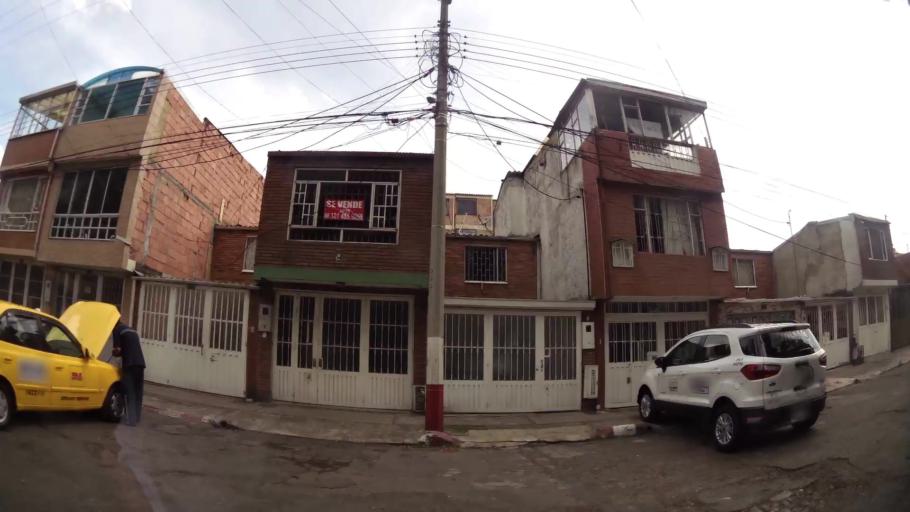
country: CO
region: Bogota D.C.
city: Bogota
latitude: 4.6969
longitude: -74.1122
